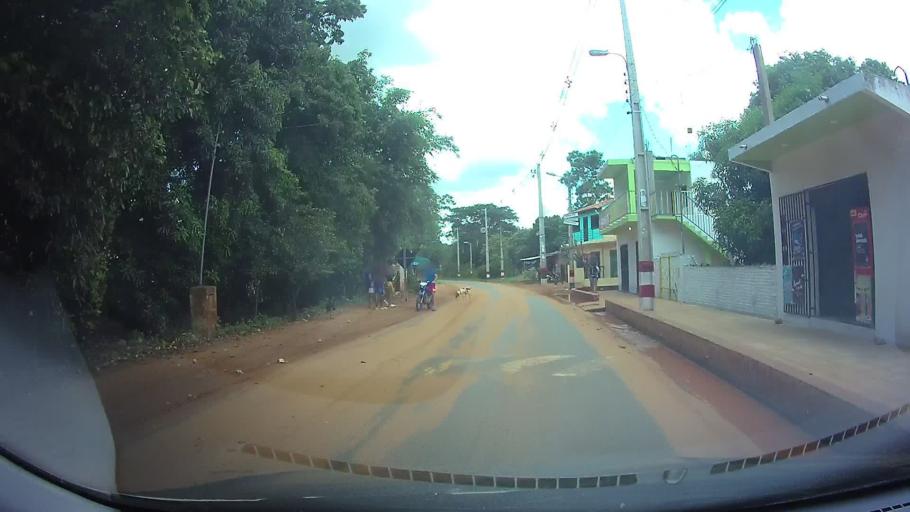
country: PY
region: Central
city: Capiata
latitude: -25.3347
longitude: -57.4196
